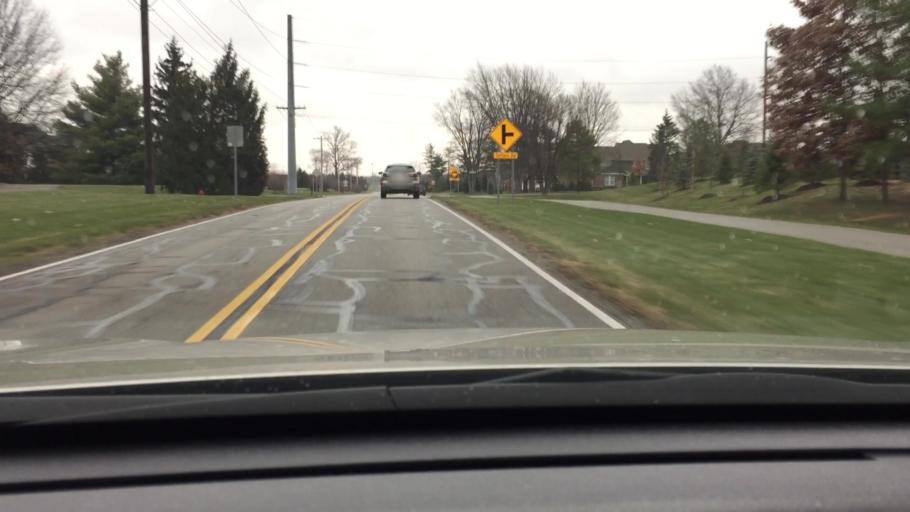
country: US
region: Indiana
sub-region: Hamilton County
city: Carmel
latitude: 40.0076
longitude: -86.1006
